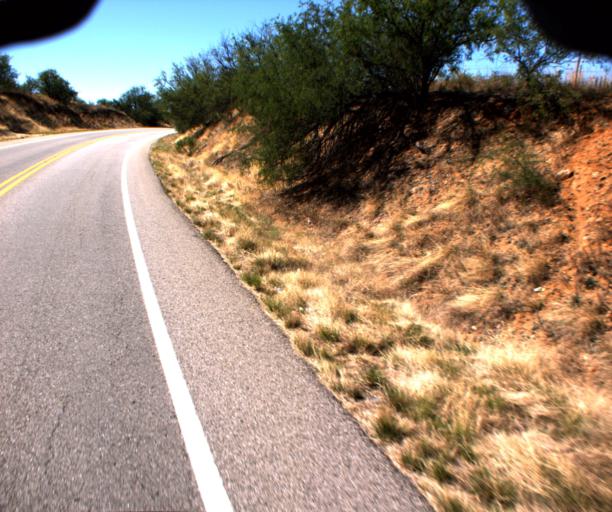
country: US
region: Arizona
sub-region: Santa Cruz County
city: Nogales
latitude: 31.4302
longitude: -110.8425
